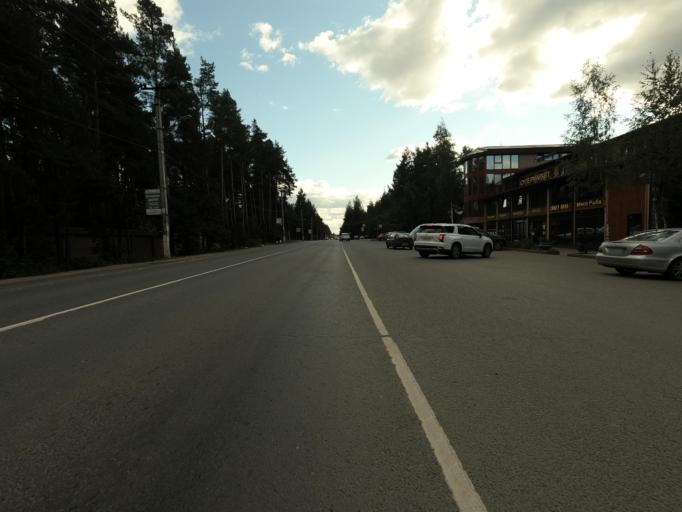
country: RU
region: Leningrad
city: Vsevolozhsk
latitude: 59.9983
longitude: 30.6609
